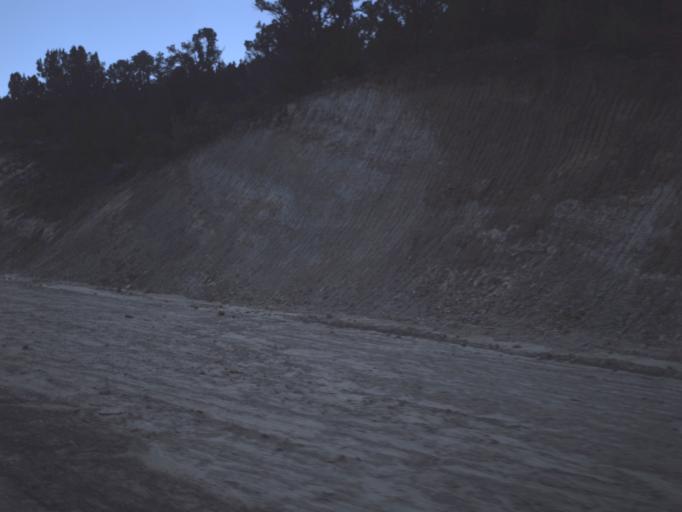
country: US
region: Utah
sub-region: Washington County
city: Enterprise
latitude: 37.5272
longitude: -113.6466
